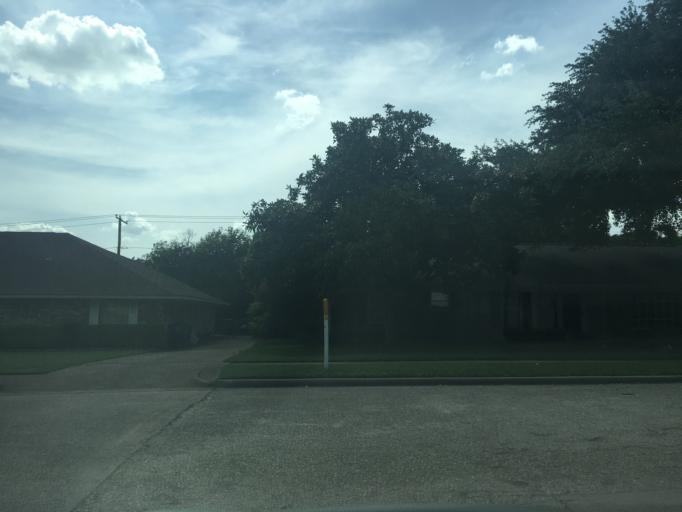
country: US
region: Texas
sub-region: Dallas County
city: Addison
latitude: 32.9197
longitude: -96.8364
